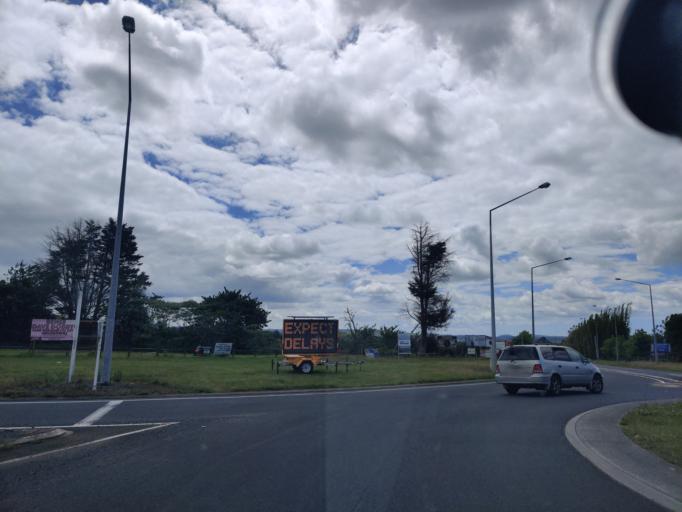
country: NZ
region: Northland
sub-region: Far North District
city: Kerikeri
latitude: -35.2539
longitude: 173.9319
